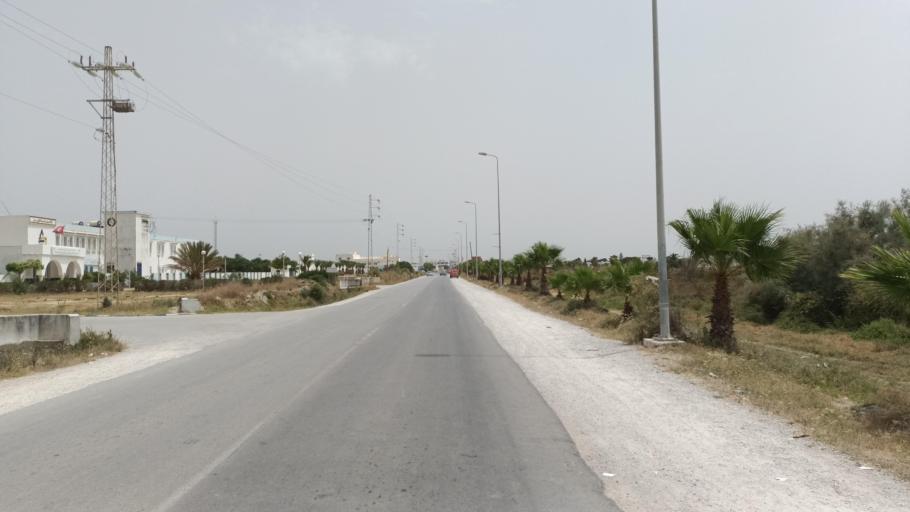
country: TN
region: Nabul
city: Manzil Bu Zalafah
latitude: 36.7130
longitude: 10.4806
